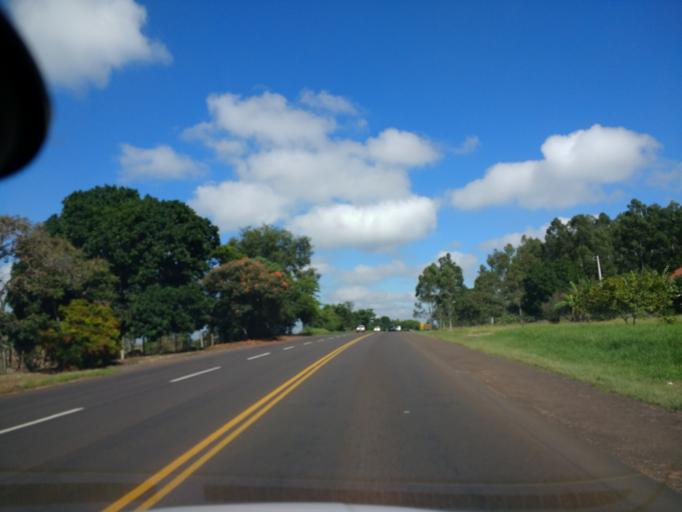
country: BR
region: Parana
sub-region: Cianorte
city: Cianorte
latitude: -23.7045
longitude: -52.6463
